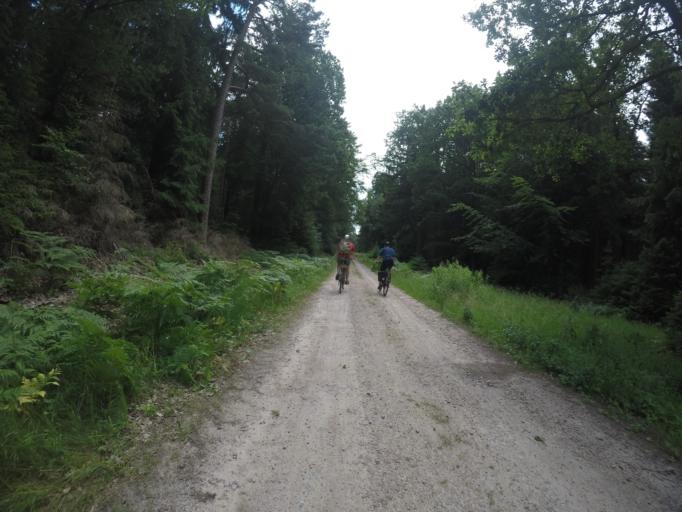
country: DE
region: Lower Saxony
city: Undeloh
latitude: 53.2378
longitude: 9.9625
